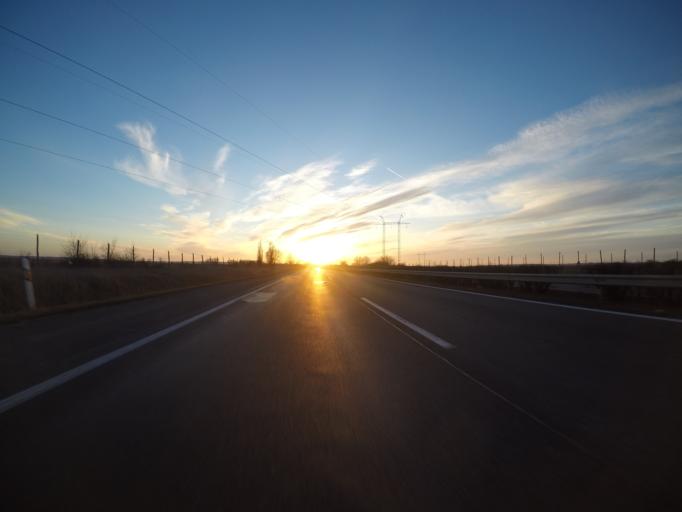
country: HU
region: Pest
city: Kartal
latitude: 47.6539
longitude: 19.5718
